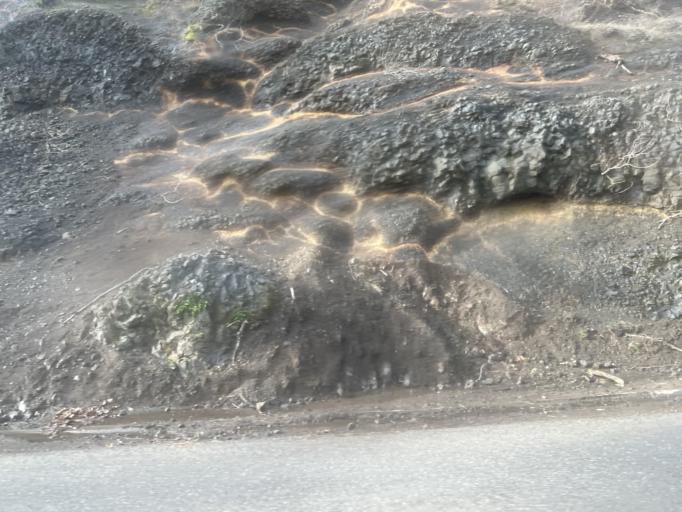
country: US
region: Washington
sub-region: Clark County
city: Washougal
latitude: 45.5374
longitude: -122.2388
